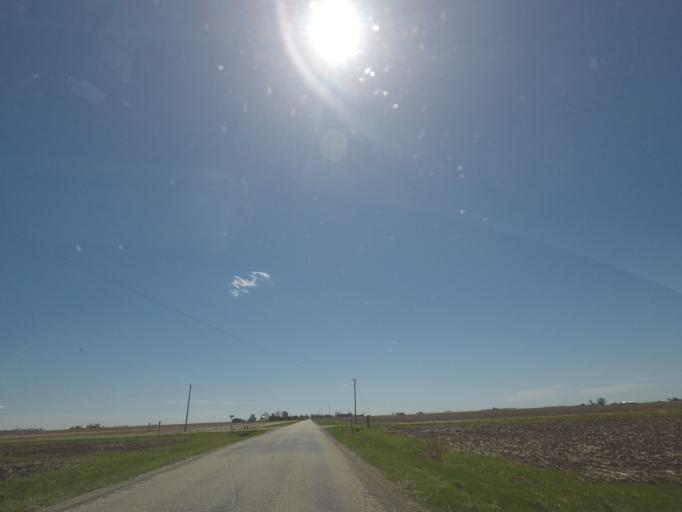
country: US
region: Illinois
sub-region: Logan County
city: Atlanta
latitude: 40.1653
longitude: -89.1936
